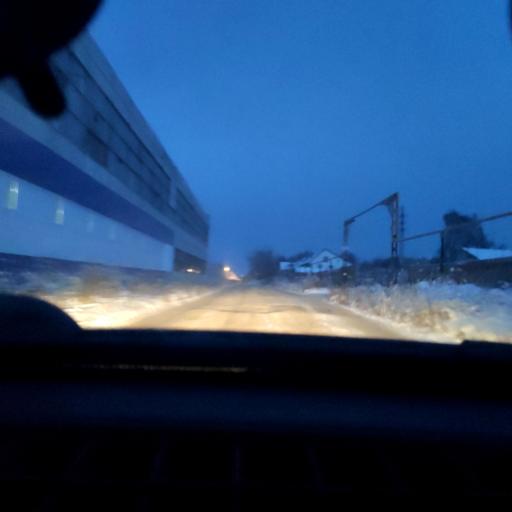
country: RU
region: Bashkortostan
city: Iglino
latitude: 54.7802
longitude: 56.2205
